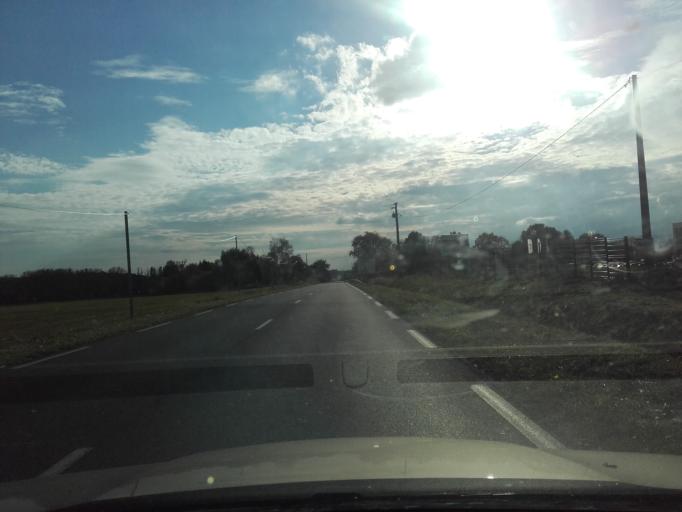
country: FR
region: Centre
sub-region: Departement d'Indre-et-Loire
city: Parcay-Meslay
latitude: 47.4677
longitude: 0.7492
